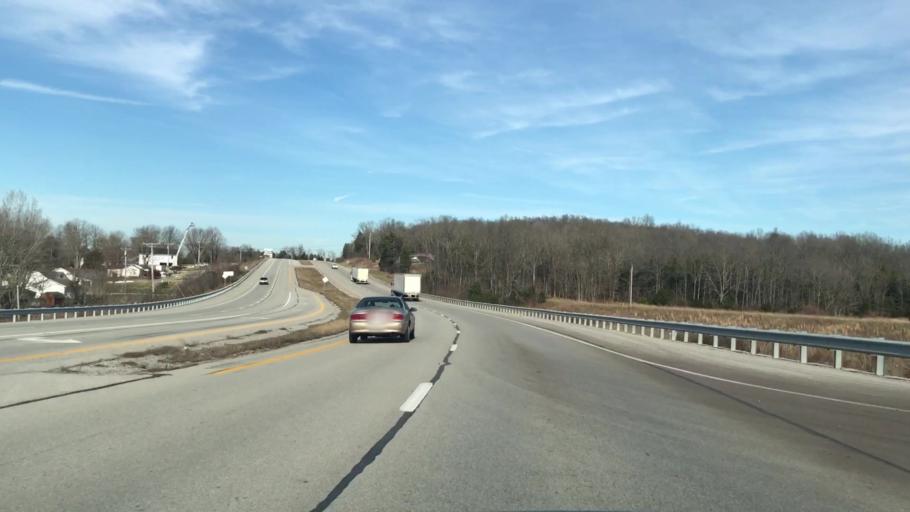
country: US
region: Kentucky
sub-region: Pulaski County
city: Somerset
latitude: 37.0074
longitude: -84.6007
